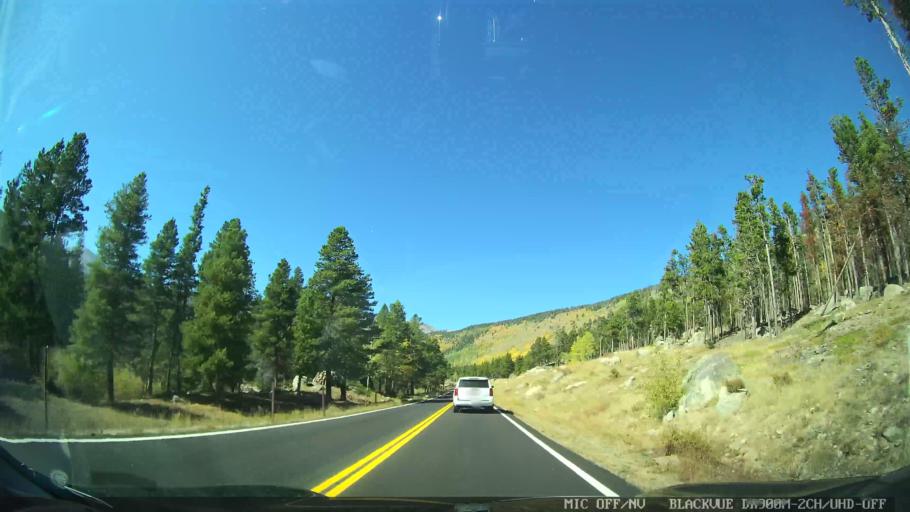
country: US
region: Colorado
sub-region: Larimer County
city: Estes Park
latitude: 40.3204
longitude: -105.6143
